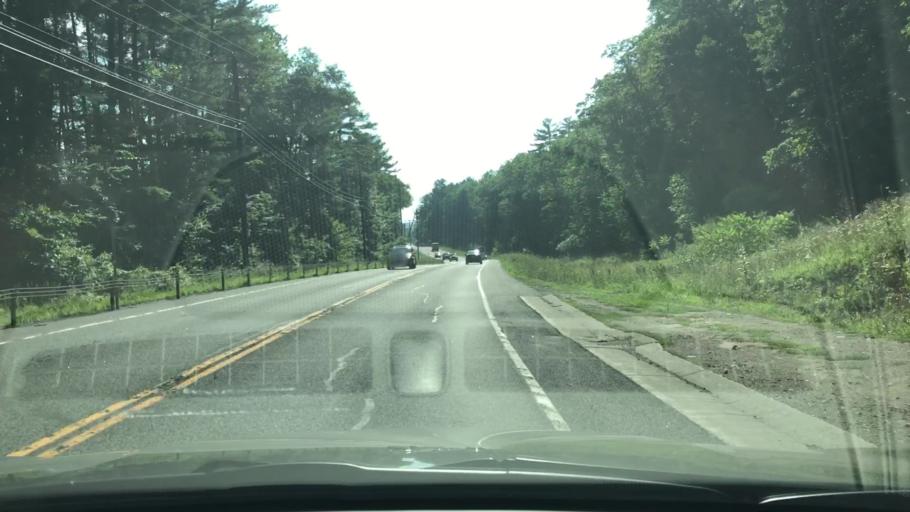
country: US
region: New York
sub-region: Warren County
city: Glens Falls North
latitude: 43.3731
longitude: -73.6822
